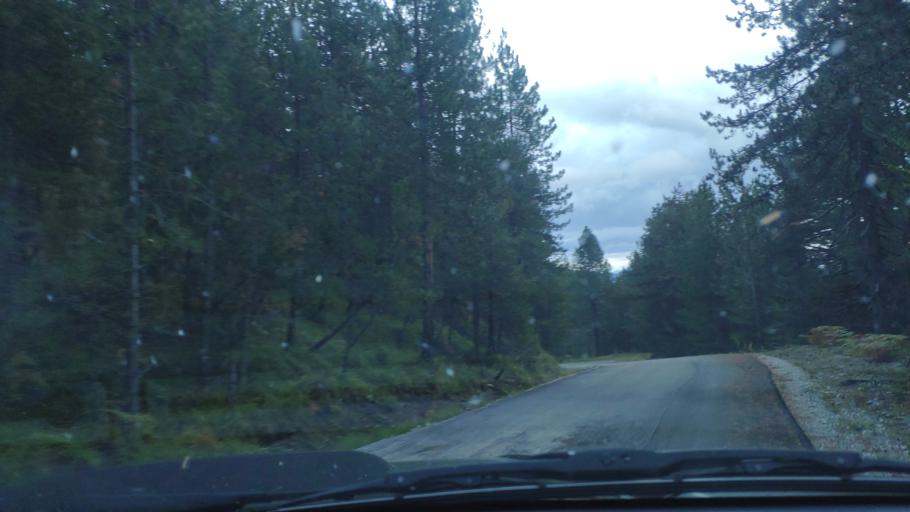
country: AL
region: Korce
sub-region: Rrethi i Kolonjes
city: Erseke
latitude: 40.2937
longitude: 20.8631
